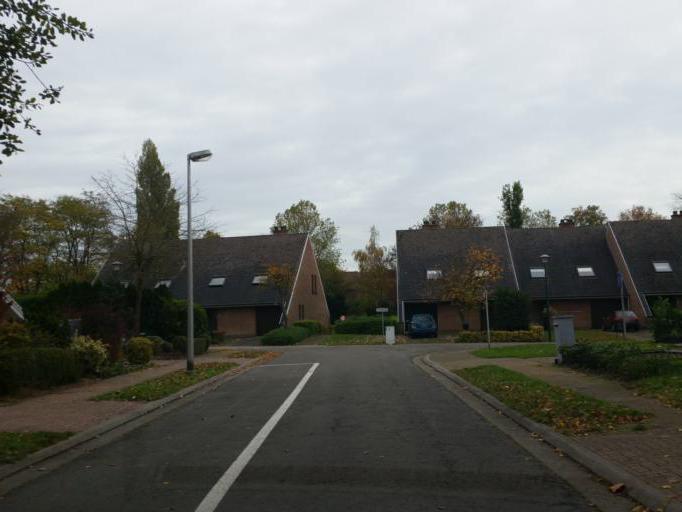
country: BE
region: Flanders
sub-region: Provincie Vlaams-Brabant
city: Machelen
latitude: 50.9176
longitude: 4.4415
